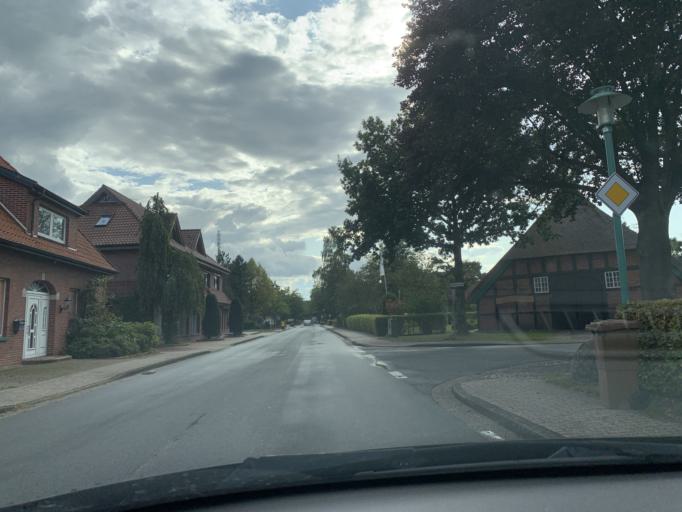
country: DE
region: Lower Saxony
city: Westerstede
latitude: 53.3150
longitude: 7.9223
